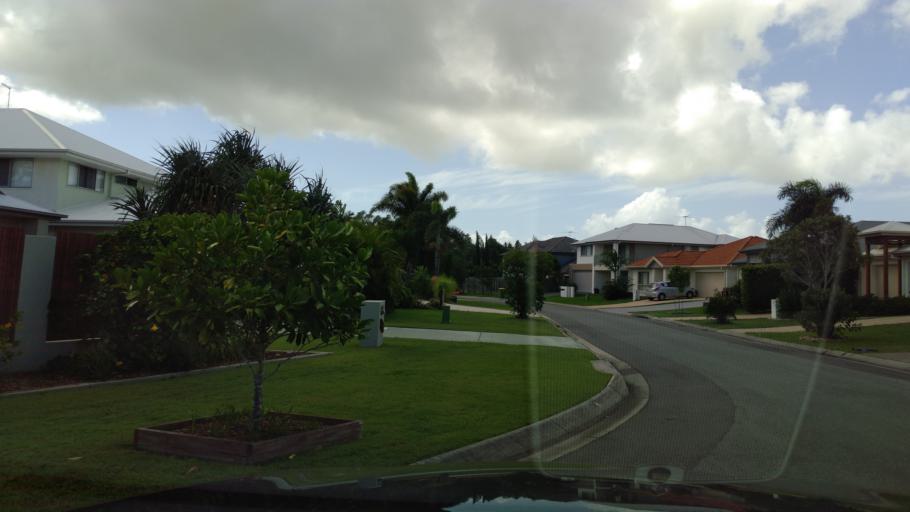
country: AU
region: Queensland
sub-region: Moreton Bay
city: Deception Bay
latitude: -27.2113
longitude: 153.0235
